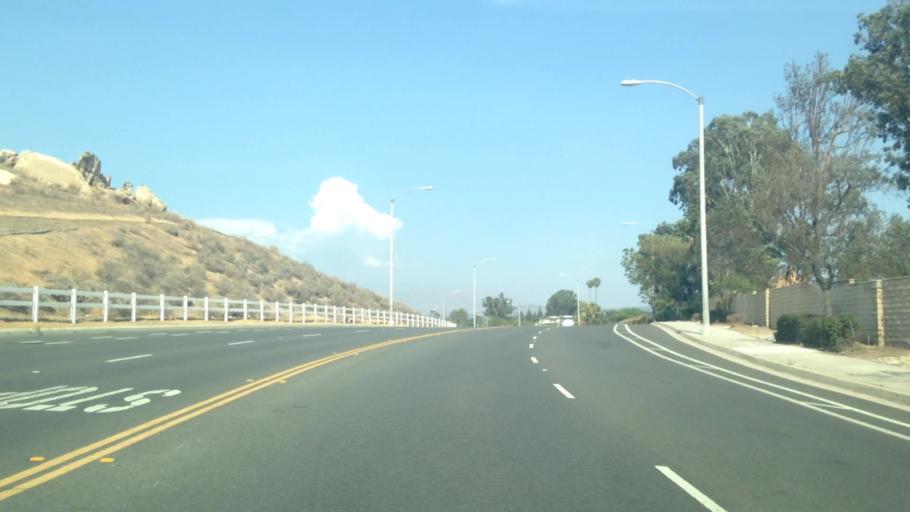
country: US
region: California
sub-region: Riverside County
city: Pedley
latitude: 33.9247
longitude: -117.4592
